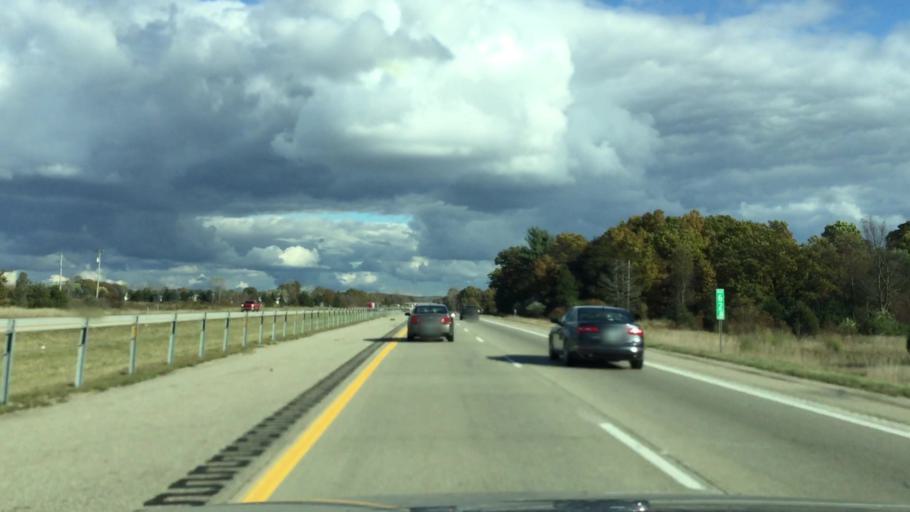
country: US
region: Michigan
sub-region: Van Buren County
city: Paw Paw
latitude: 42.2180
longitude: -85.8445
